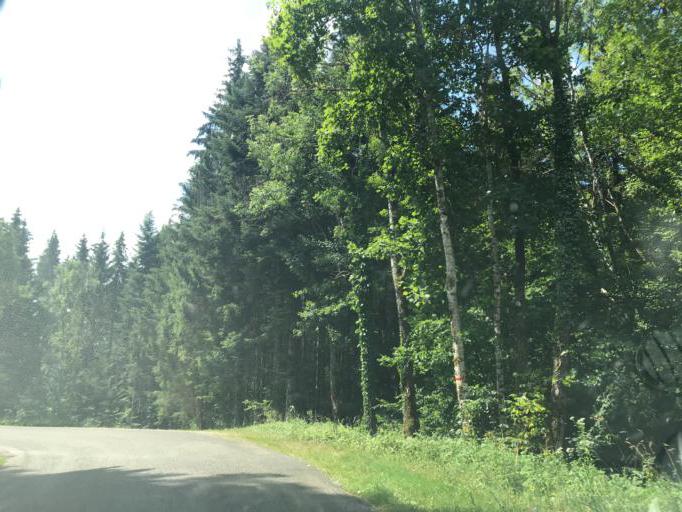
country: FR
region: Franche-Comte
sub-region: Departement du Jura
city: Moirans-en-Montagne
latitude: 46.4935
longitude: 5.7762
